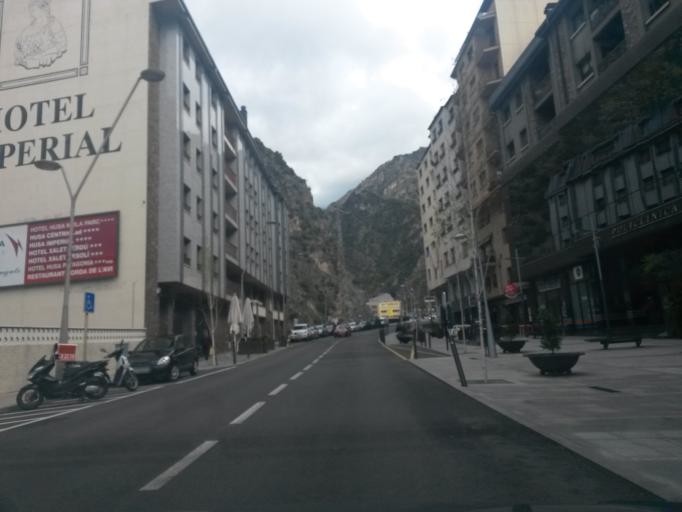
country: AD
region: Sant Julia de Loria
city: Sant Julia de Loria
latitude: 42.4691
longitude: 1.4927
